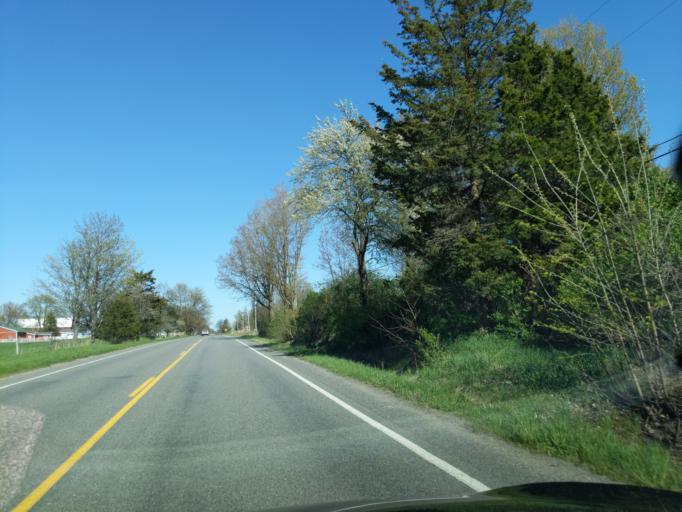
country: US
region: Michigan
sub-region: Kent County
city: Forest Hills
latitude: 42.8853
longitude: -85.4354
